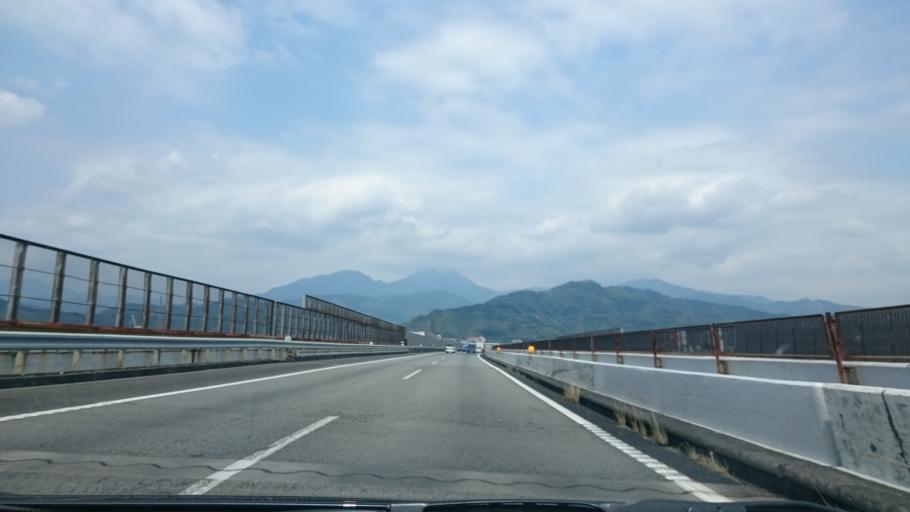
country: JP
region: Shizuoka
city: Shizuoka-shi
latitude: 34.9971
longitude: 138.4340
